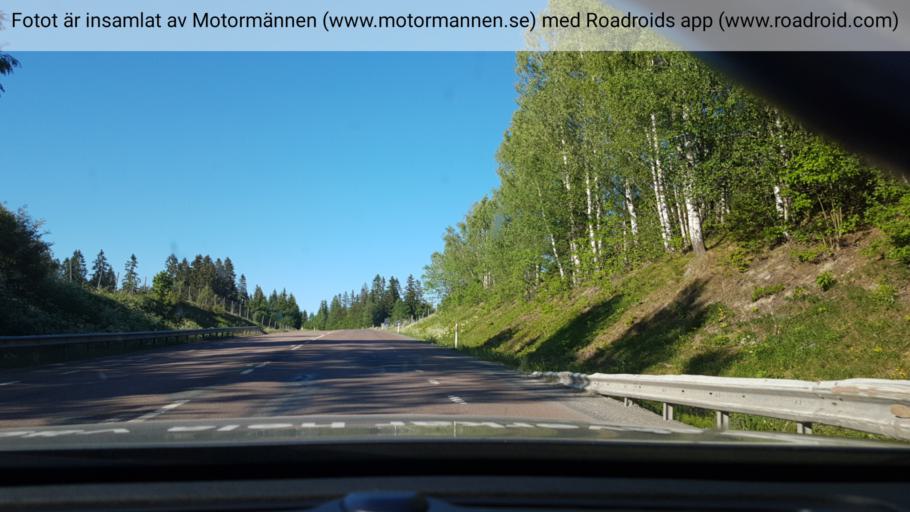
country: SE
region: Vaesternorrland
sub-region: Haernoesands Kommun
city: Haernoesand
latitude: 62.6884
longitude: 17.8490
